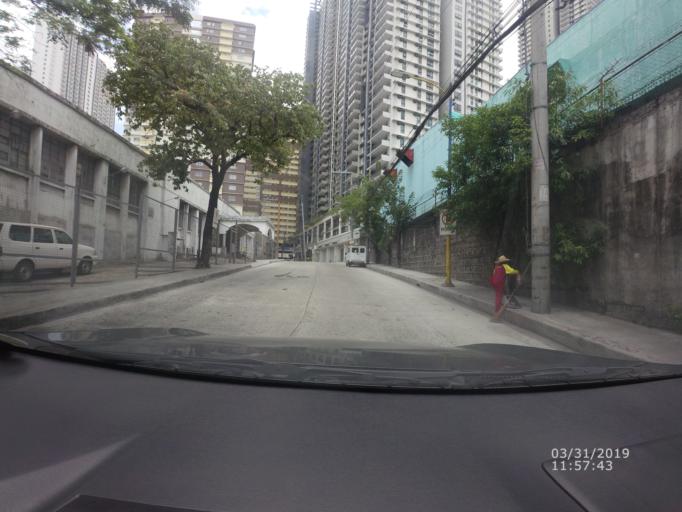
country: PH
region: Metro Manila
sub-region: Mandaluyong
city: Mandaluyong City
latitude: 14.5738
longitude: 121.0514
